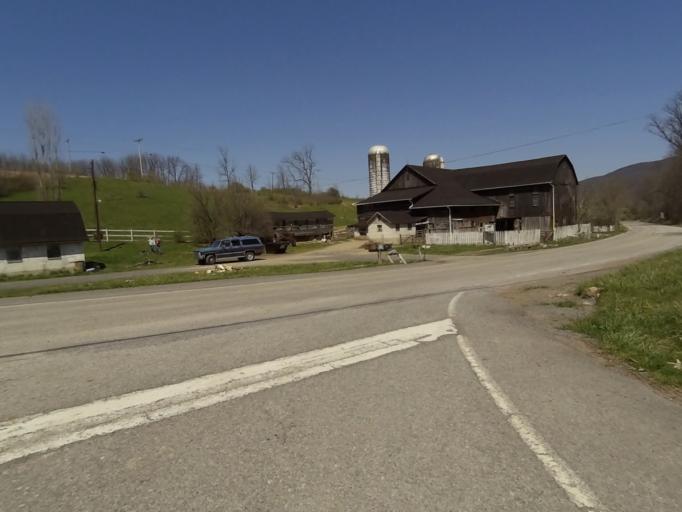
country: US
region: Pennsylvania
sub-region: Blair County
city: Williamsburg
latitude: 40.5611
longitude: -78.1551
